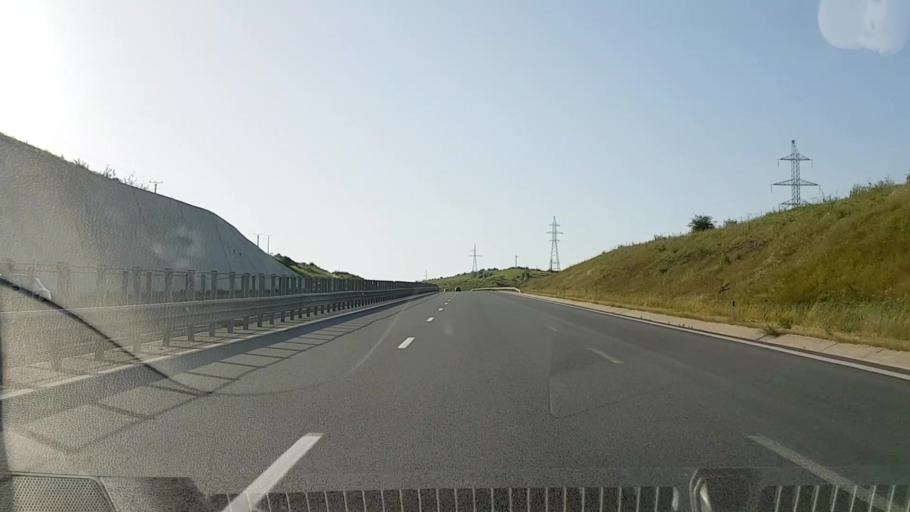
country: RO
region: Cluj
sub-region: Comuna Sandulesti
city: Sandulesti
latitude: 46.5967
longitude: 23.7103
